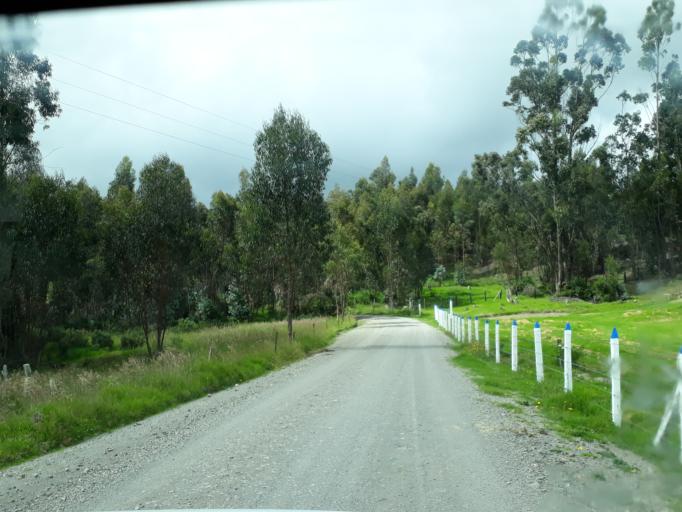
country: CO
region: Cundinamarca
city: La Mesa
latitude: 5.2809
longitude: -73.9089
